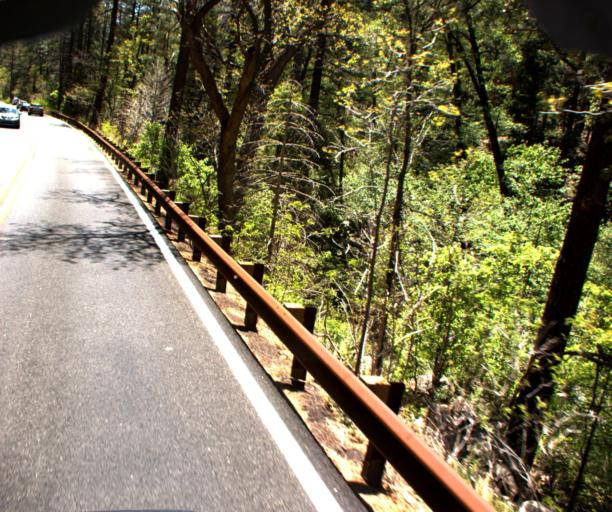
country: US
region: Arizona
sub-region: Coconino County
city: Kachina Village
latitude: 35.0192
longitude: -111.7371
